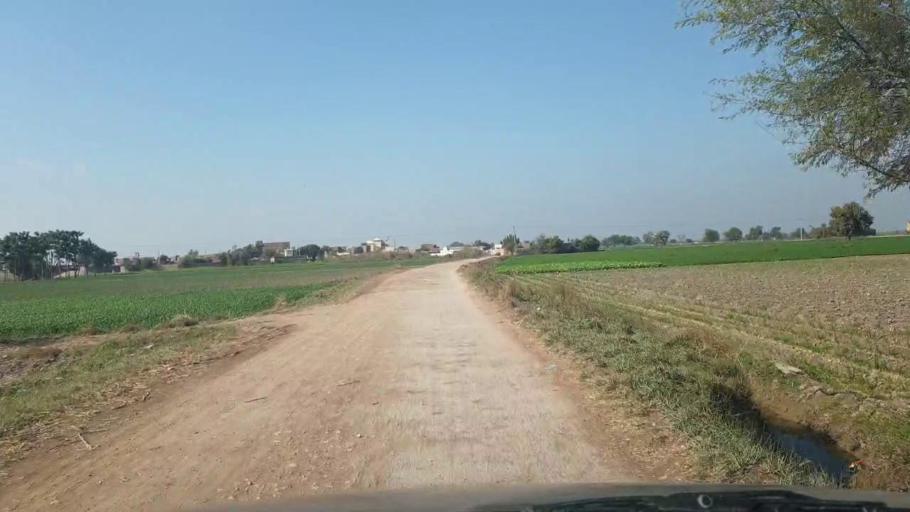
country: PK
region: Sindh
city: Bhit Shah
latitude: 25.8867
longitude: 68.5297
